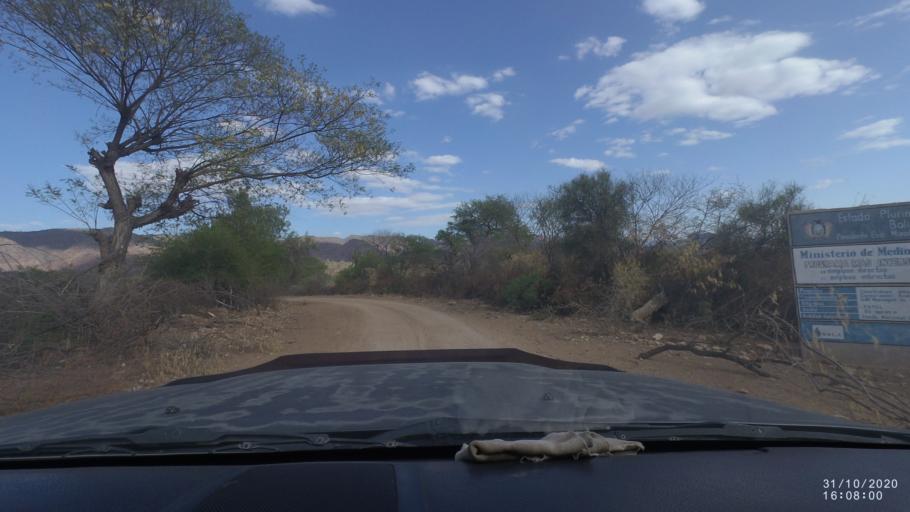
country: BO
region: Chuquisaca
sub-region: Provincia Zudanez
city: Mojocoya
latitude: -18.3836
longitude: -64.6433
